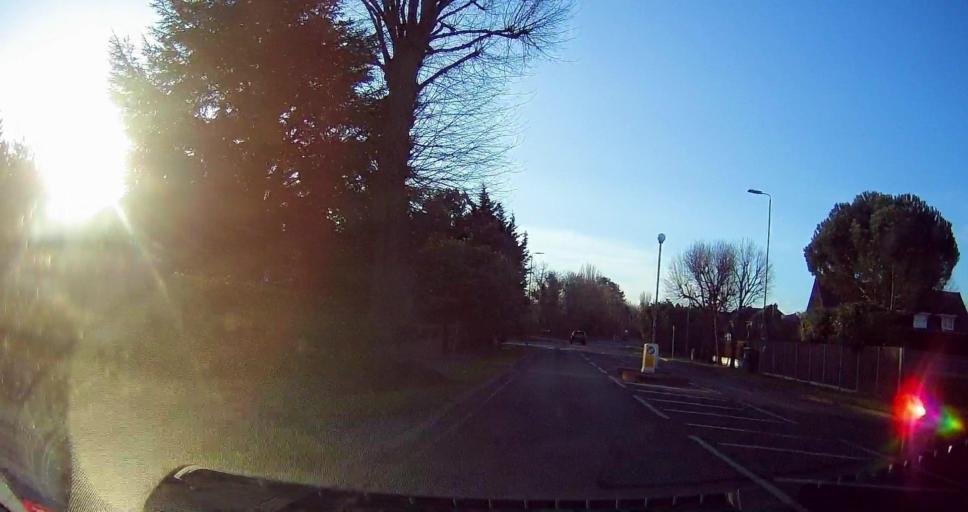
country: GB
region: England
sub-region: Greater London
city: Chislehurst
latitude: 51.4000
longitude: 0.0558
